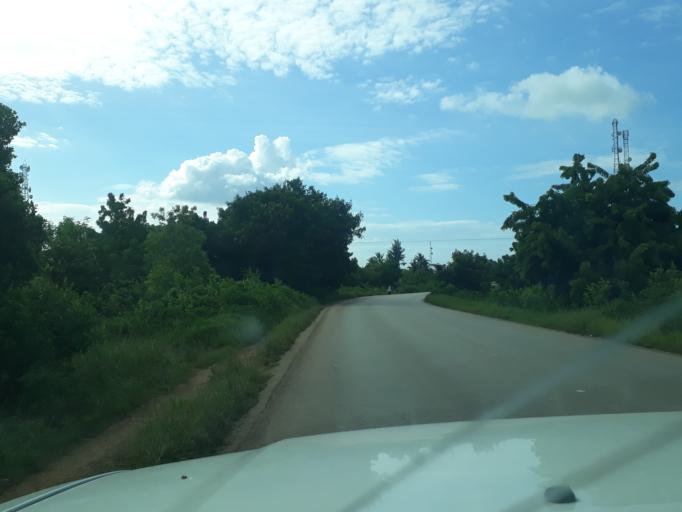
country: TZ
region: Zanzibar North
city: Nungwi
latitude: -5.7652
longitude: 39.3012
